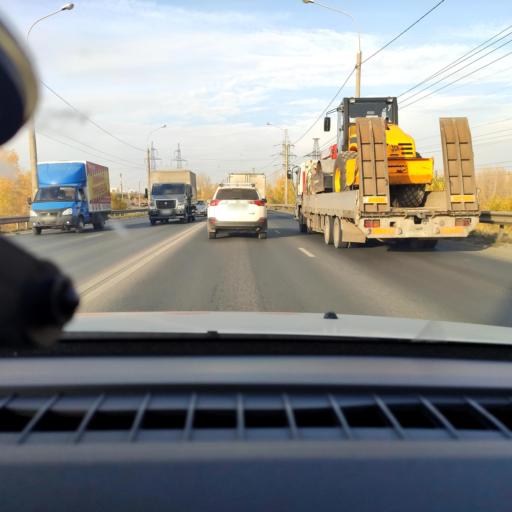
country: RU
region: Samara
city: Samara
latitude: 53.1637
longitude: 50.1961
